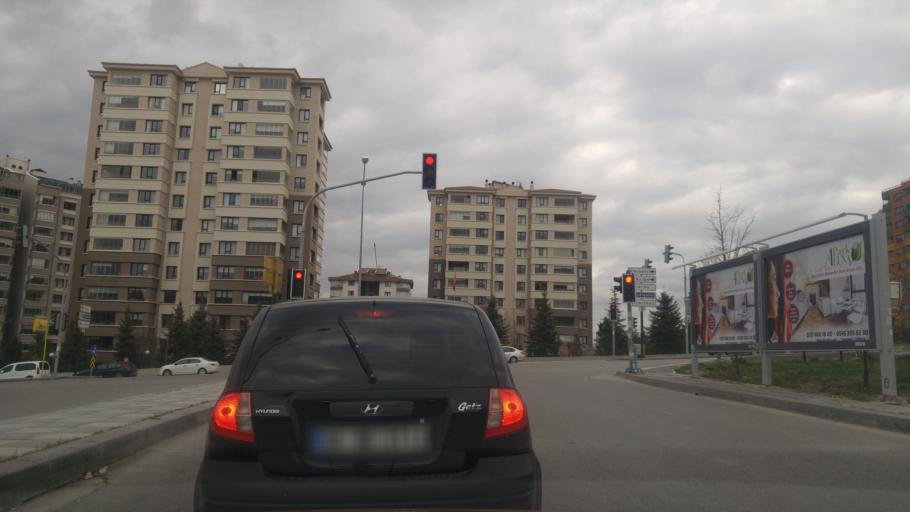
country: TR
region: Ankara
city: Etimesgut
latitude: 39.8664
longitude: 32.6433
